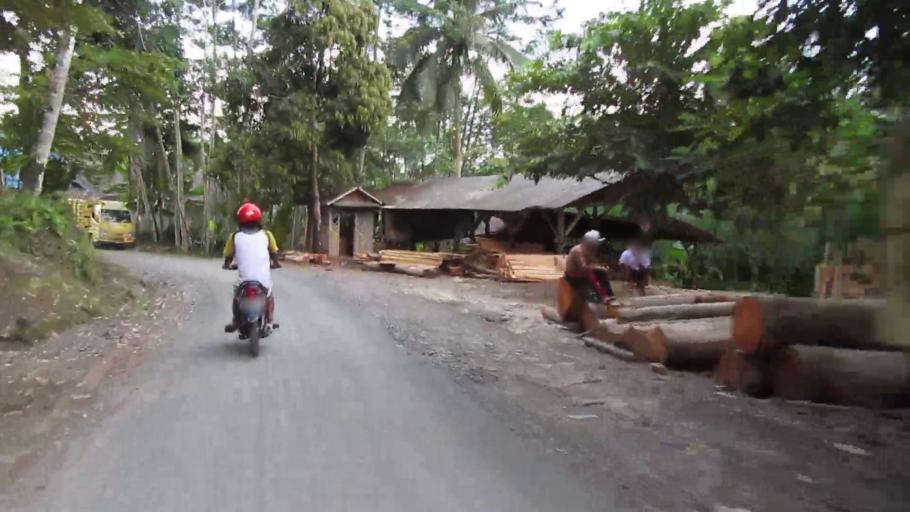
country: ID
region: West Java
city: Mandala
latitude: -7.7354
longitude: 108.4743
